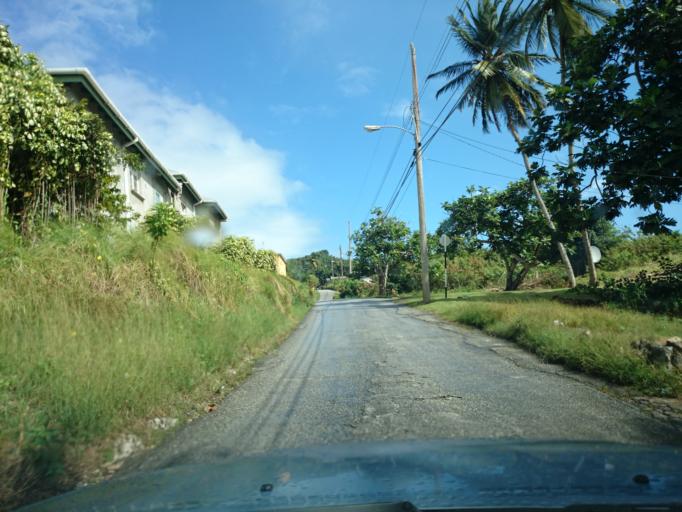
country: BB
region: Saint Peter
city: Speightstown
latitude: 13.2283
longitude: -59.6259
